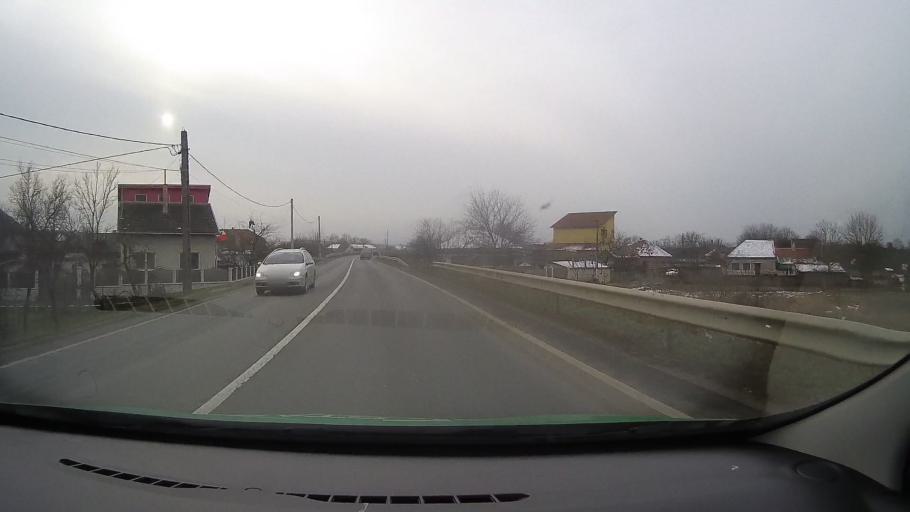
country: RO
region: Hunedoara
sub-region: Comuna Rapoltu Mare
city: Rapoltu Mare
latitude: 45.8364
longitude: 23.0518
